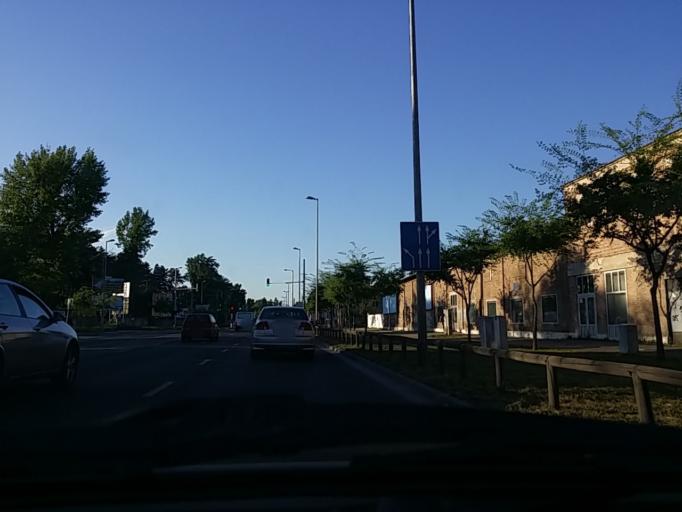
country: HU
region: Budapest
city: Budapest IV. keruelet
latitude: 47.5842
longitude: 19.0819
